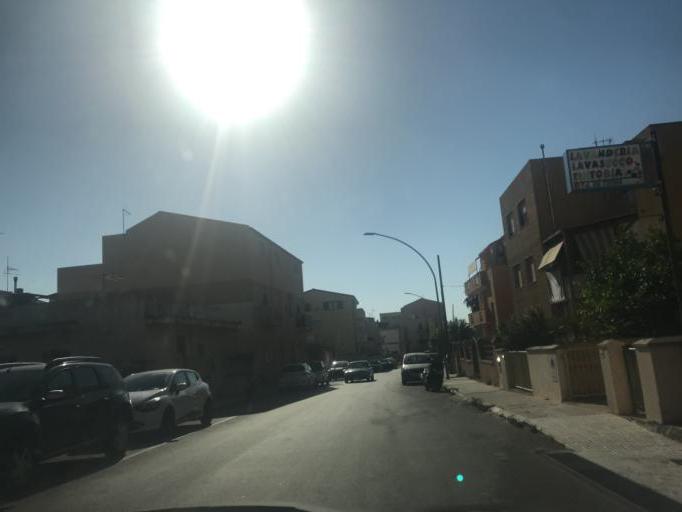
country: IT
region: Sardinia
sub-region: Provincia di Sassari
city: Alghero
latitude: 40.5558
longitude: 8.3293
